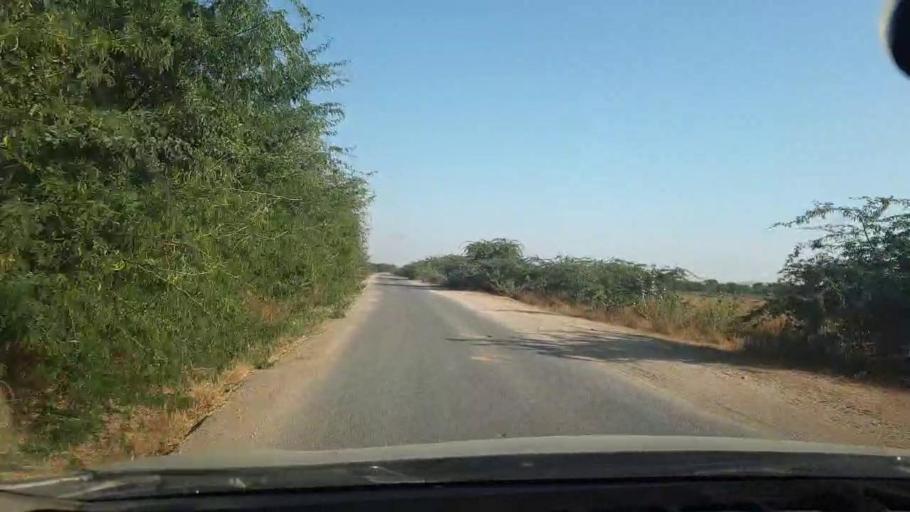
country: PK
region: Sindh
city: Malir Cantonment
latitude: 25.1642
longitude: 67.1958
